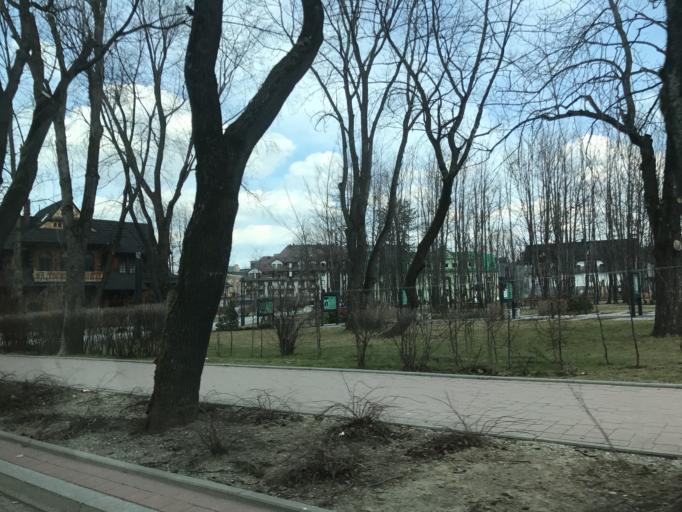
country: PL
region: Lesser Poland Voivodeship
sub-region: Powiat tatrzanski
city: Zakopane
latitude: 49.2909
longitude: 19.9543
